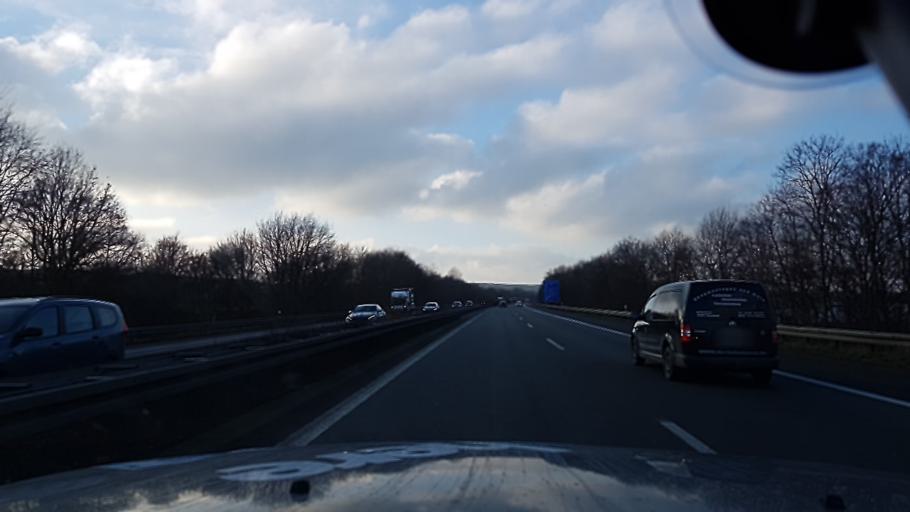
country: DE
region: North Rhine-Westphalia
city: Ibbenburen
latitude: 52.2577
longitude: 7.7300
